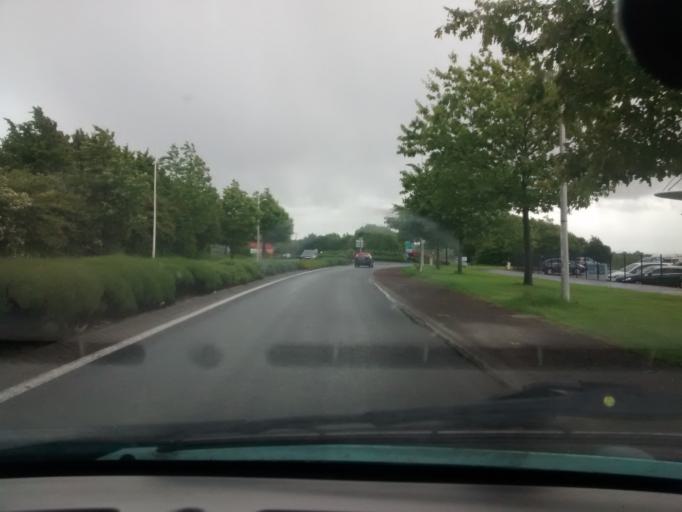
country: FR
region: Lower Normandy
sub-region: Departement de la Manche
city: Saint-Lo
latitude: 49.1016
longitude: -1.0623
